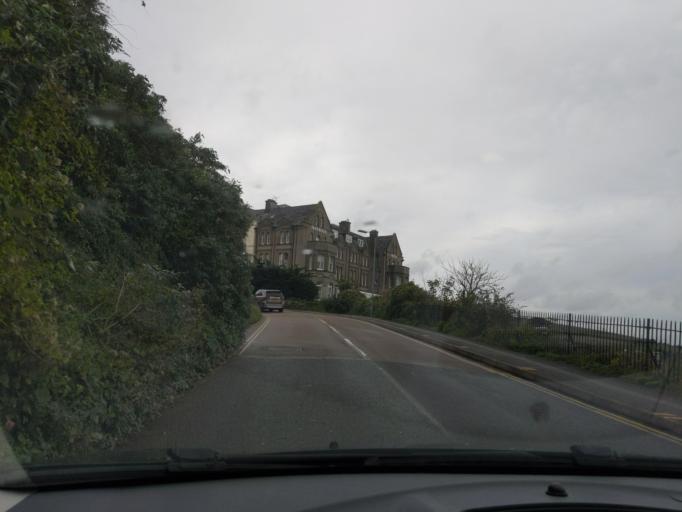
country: GB
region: England
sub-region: Cornwall
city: Padstow
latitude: 50.5391
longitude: -4.9365
